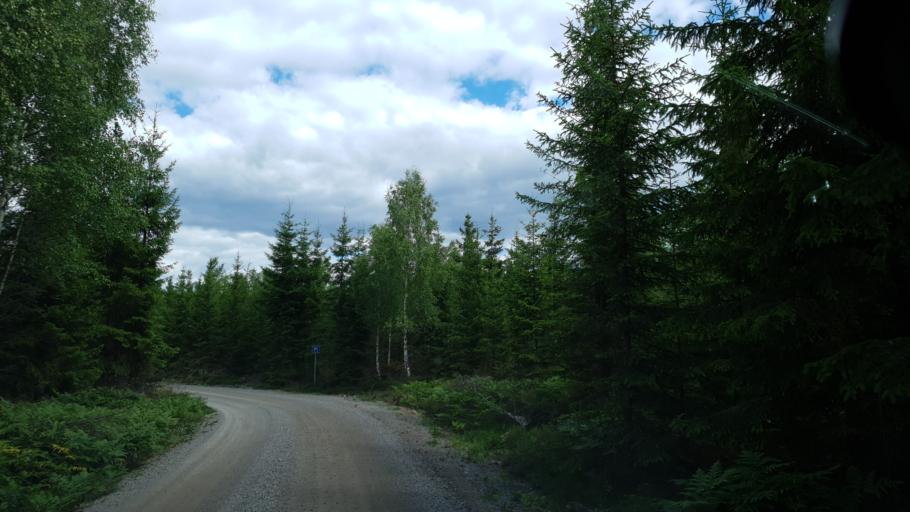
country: SE
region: Kalmar
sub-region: Hultsfreds Kommun
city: Virserum
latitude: 57.0869
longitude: 15.6202
